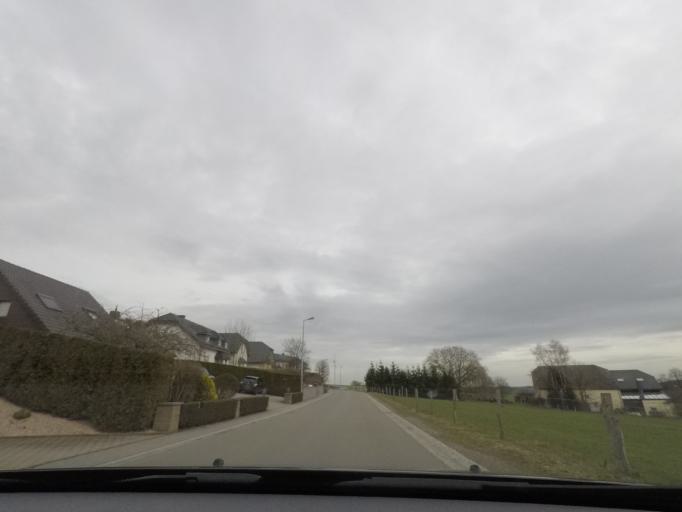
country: LU
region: Diekirch
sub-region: Canton de Wiltz
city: Winseler
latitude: 50.0158
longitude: 5.8857
